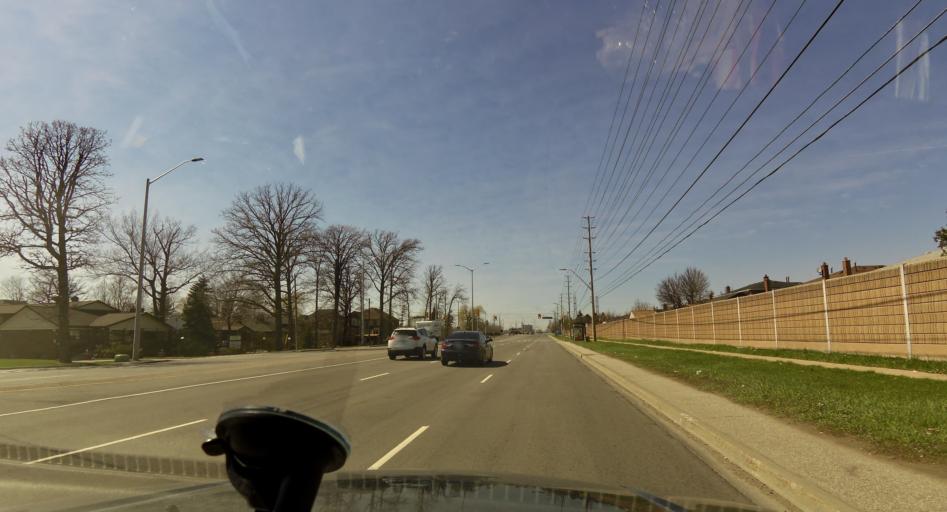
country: CA
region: Ontario
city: Etobicoke
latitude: 43.6276
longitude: -79.6094
